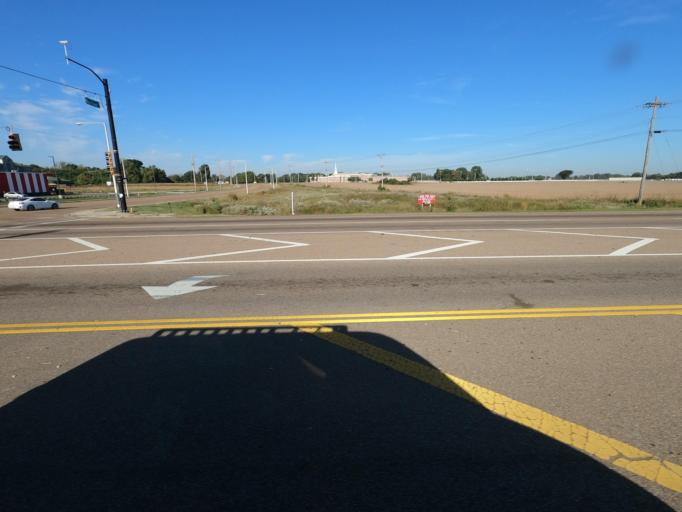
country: US
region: Tennessee
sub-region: Shelby County
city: Millington
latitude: 35.3623
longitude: -89.8907
